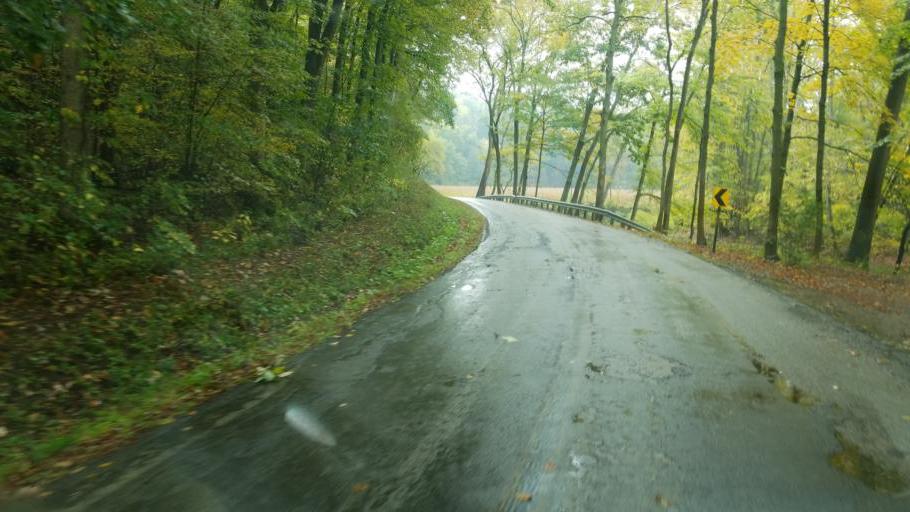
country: US
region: Ohio
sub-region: Sandusky County
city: Bellville
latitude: 40.6128
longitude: -82.3911
